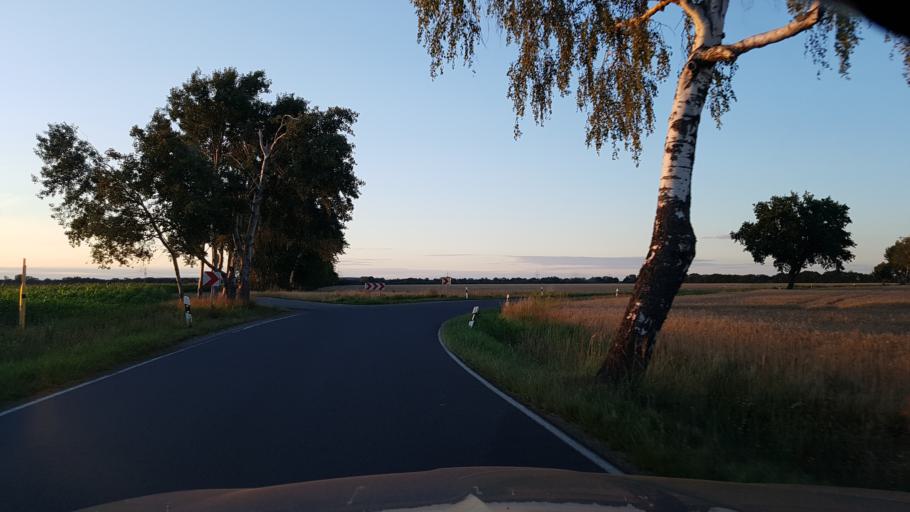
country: DE
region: Brandenburg
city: Hirschfeld
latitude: 51.4239
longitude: 13.6043
